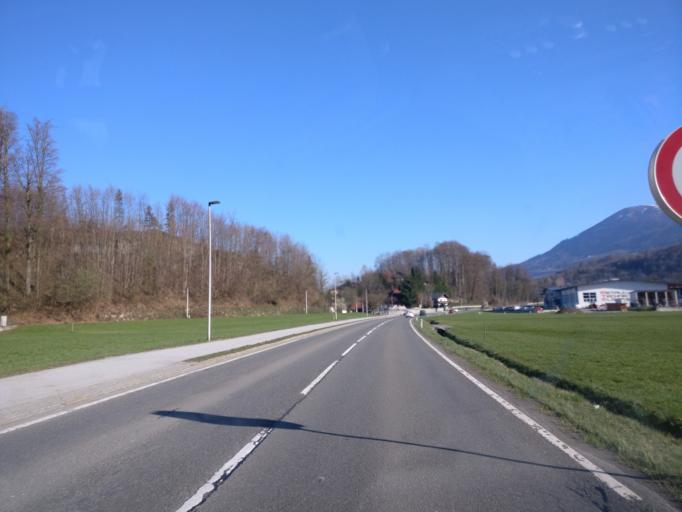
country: AT
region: Salzburg
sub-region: Politischer Bezirk Salzburg-Umgebung
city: Elsbethen
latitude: 47.7603
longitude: 13.0861
